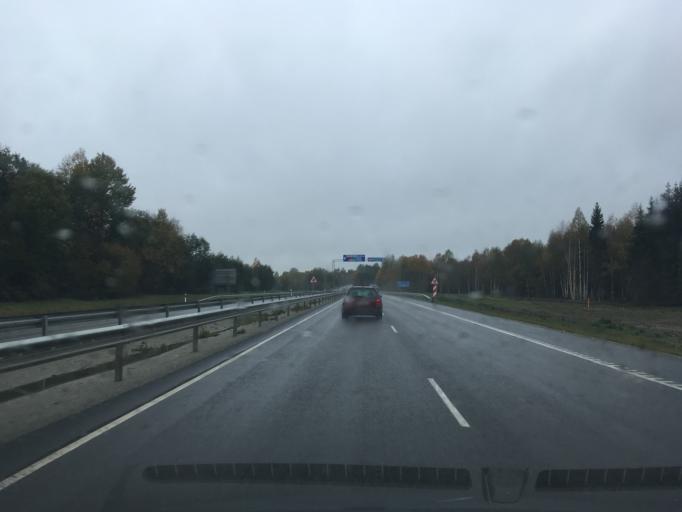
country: EE
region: Harju
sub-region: Saue linn
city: Saue
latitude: 59.3128
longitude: 24.5887
